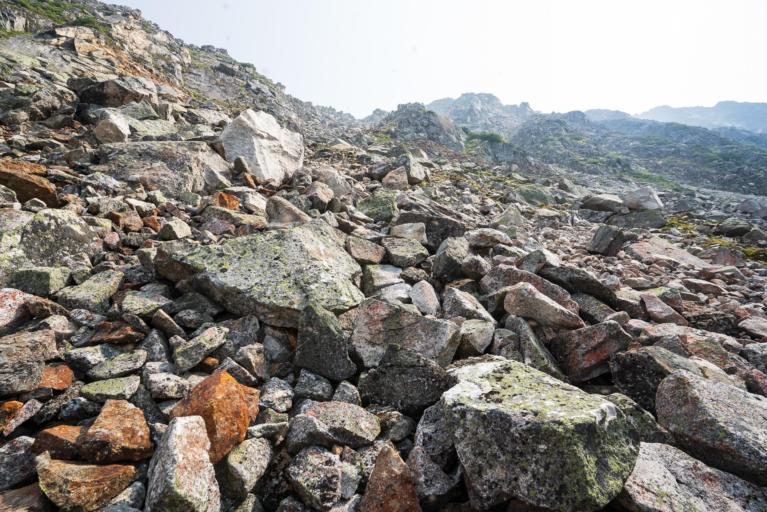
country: RU
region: Transbaikal Territory
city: Kuanda
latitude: 56.7924
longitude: 116.8128
